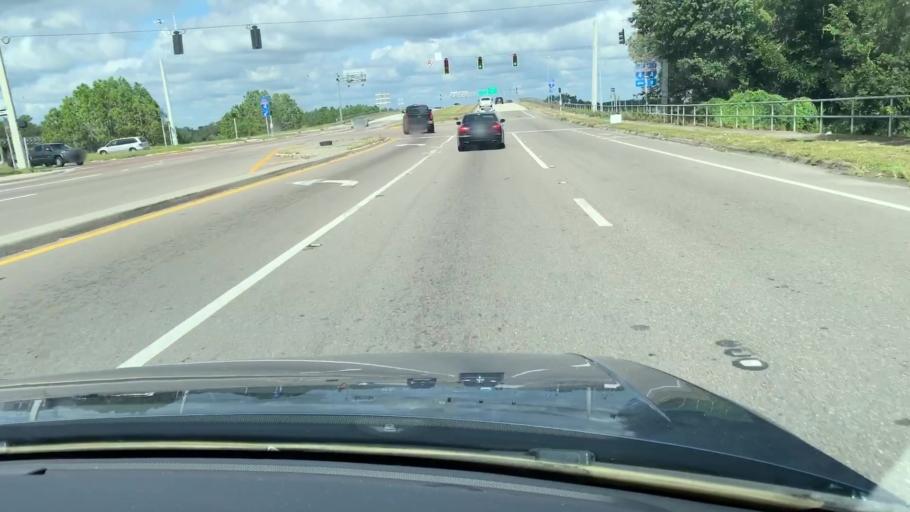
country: US
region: Florida
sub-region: Polk County
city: Winston
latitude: 28.0342
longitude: -82.0559
